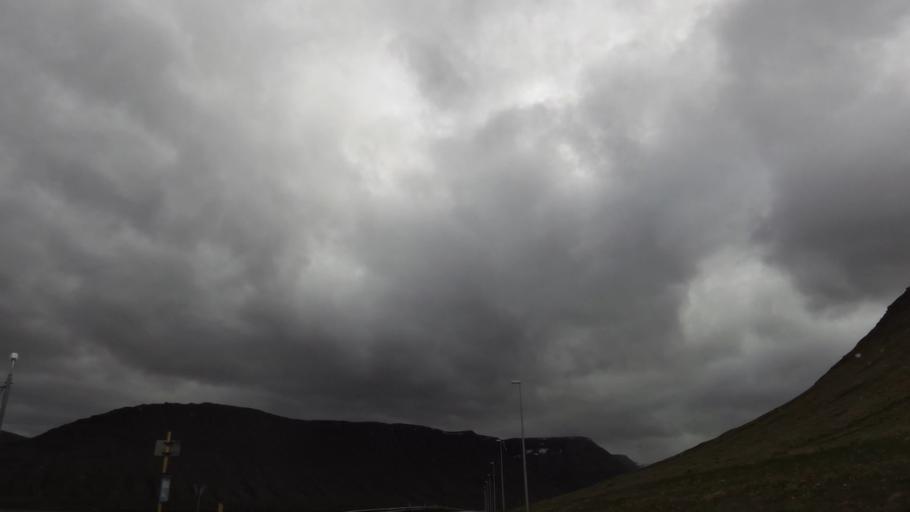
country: IS
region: Westfjords
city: Isafjoerdur
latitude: 66.1031
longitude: -23.1097
